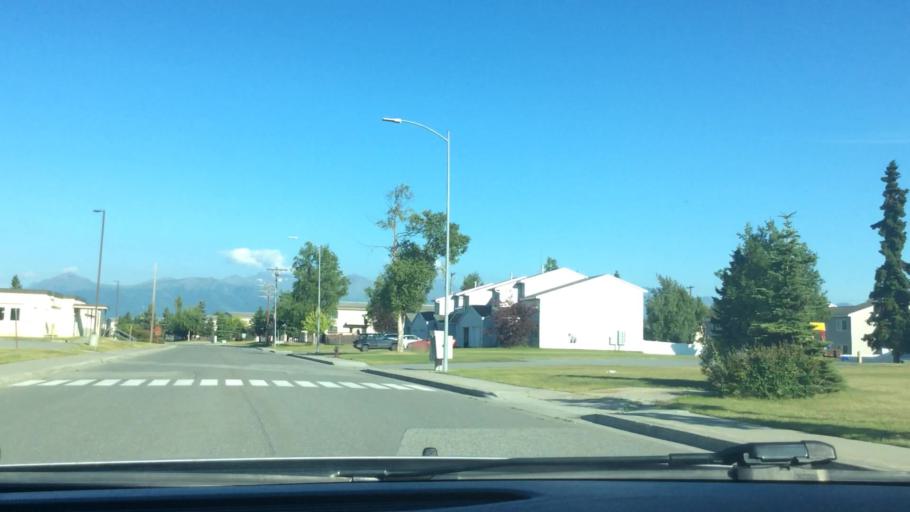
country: US
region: Alaska
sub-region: Anchorage Municipality
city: Anchorage
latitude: 61.2336
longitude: -149.8619
